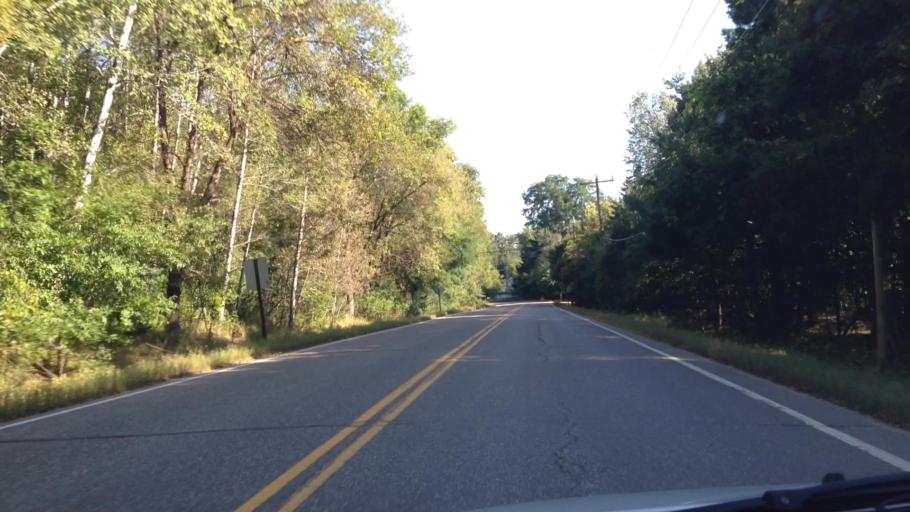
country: US
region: Minnesota
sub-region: Washington County
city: Stillwater
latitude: 45.0821
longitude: -92.8121
